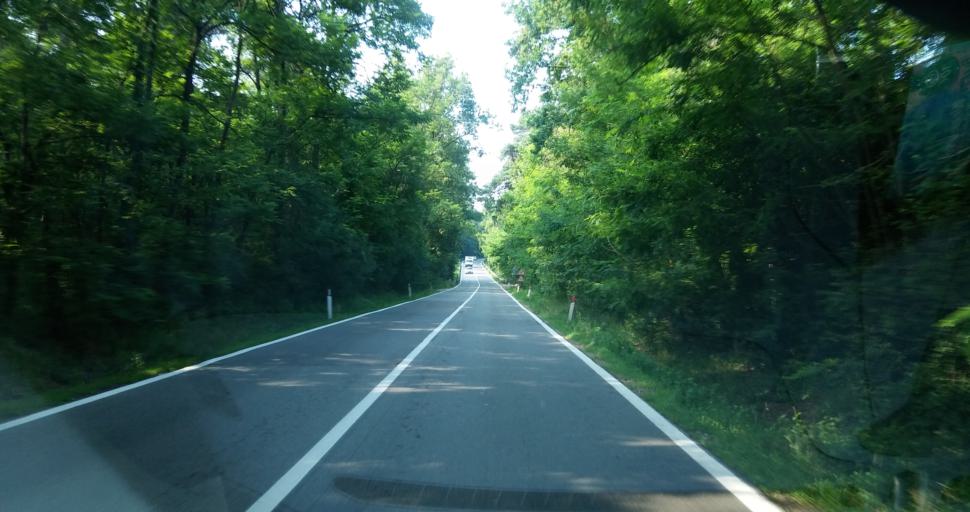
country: IT
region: Lombardy
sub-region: Provincia di Varese
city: Vizzola Ticino
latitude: 45.6534
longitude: 8.7041
